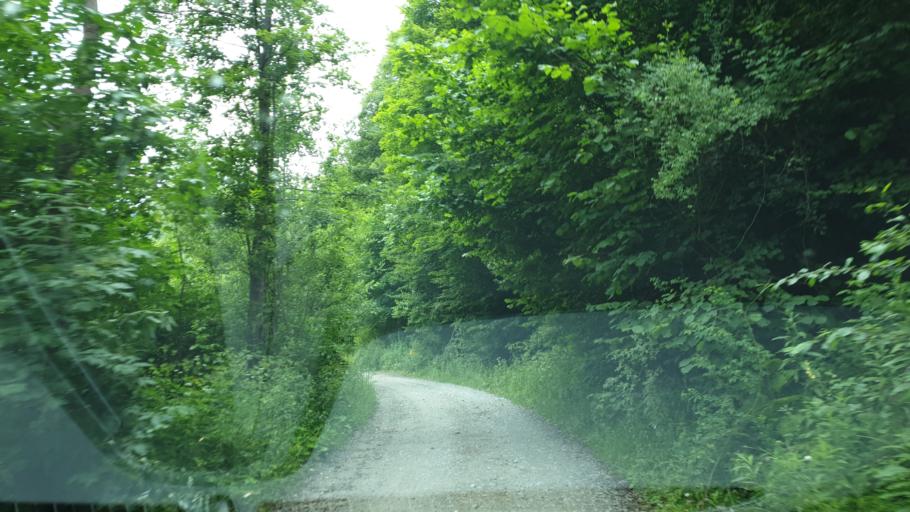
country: RO
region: Hunedoara
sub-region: Comuna Uricani
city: Uricani
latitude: 45.3008
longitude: 22.9922
